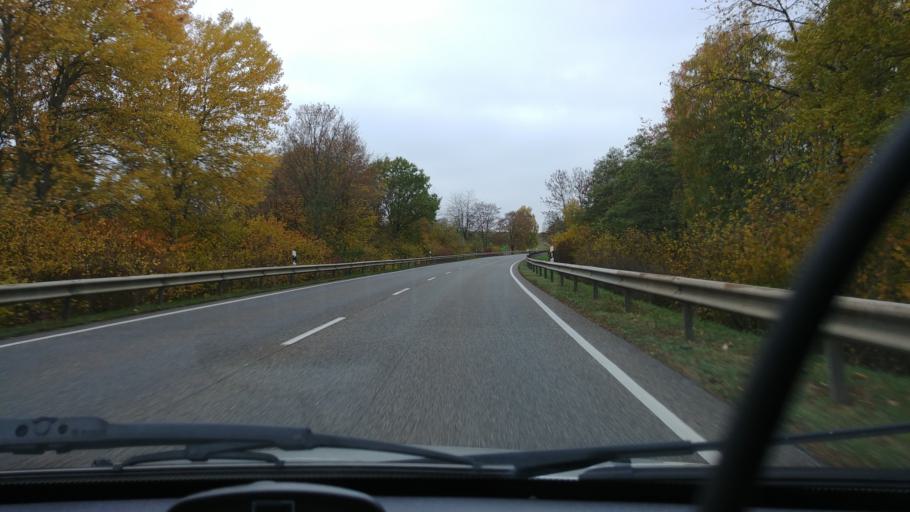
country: DE
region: Rheinland-Pfalz
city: Hachenburg
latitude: 50.6693
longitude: 7.8149
